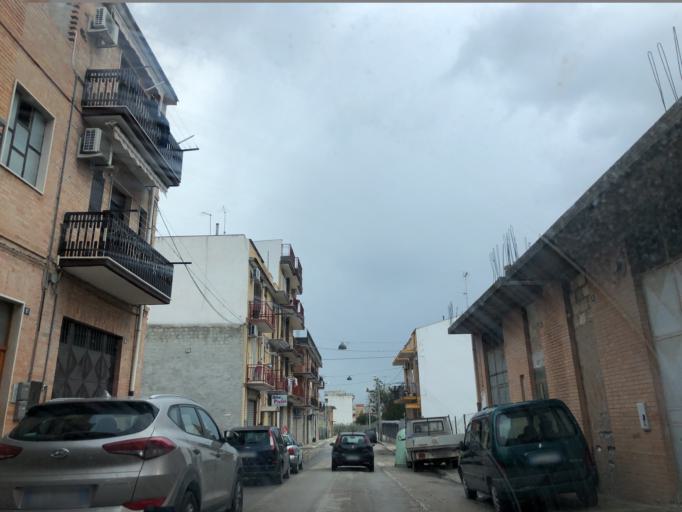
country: IT
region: Apulia
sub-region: Provincia di Foggia
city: Lucera
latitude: 41.5032
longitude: 15.3416
